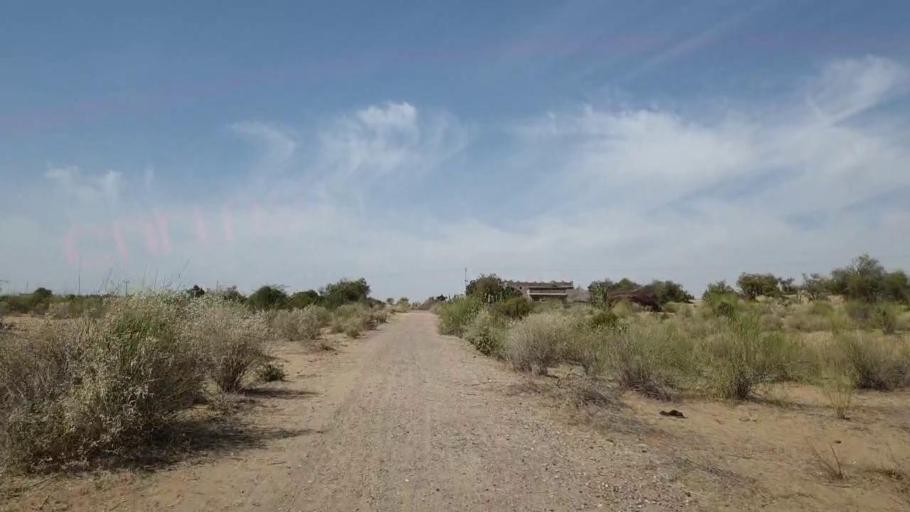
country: PK
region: Sindh
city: Umarkot
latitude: 25.1952
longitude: 69.8978
